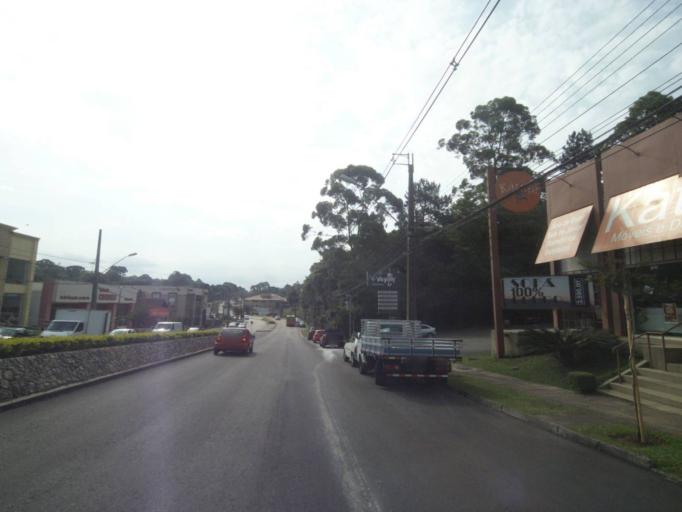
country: BR
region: Parana
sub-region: Curitiba
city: Curitiba
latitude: -25.4133
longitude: -49.3137
